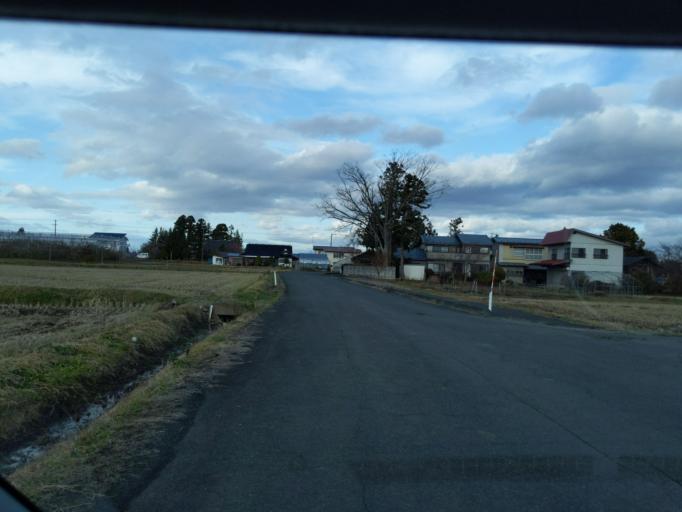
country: JP
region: Iwate
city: Mizusawa
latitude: 39.1856
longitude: 141.1022
